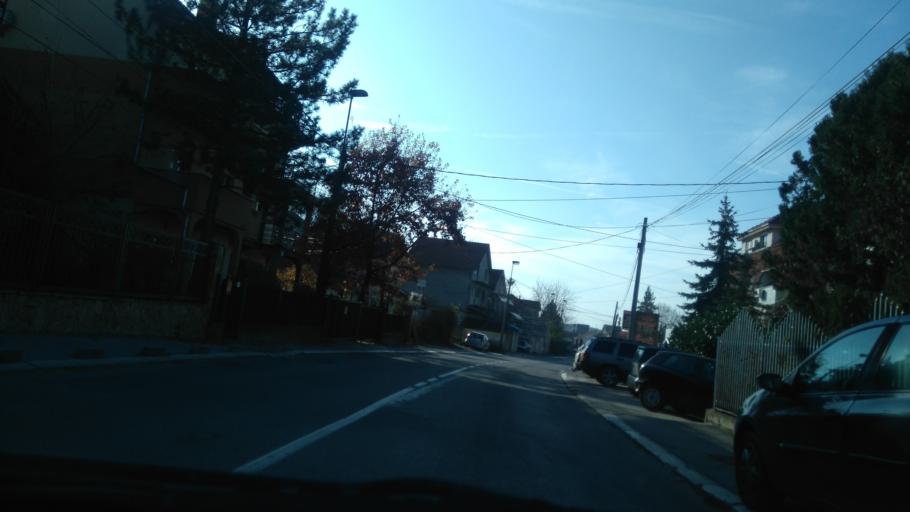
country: RS
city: Ostruznica
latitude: 44.7332
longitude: 20.3730
